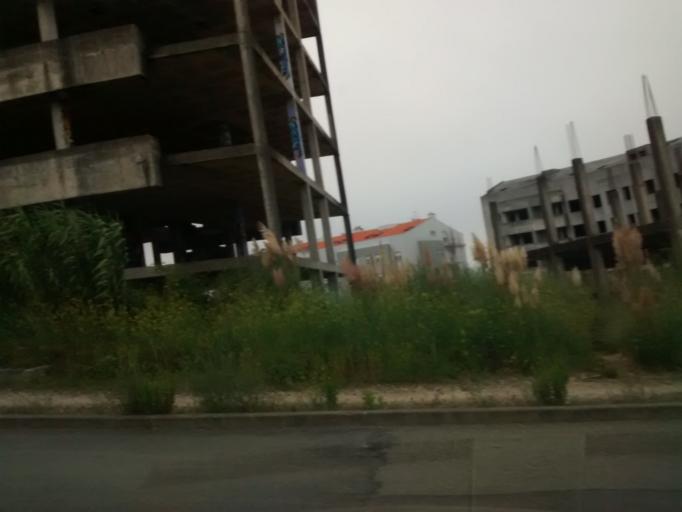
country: PT
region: Aveiro
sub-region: Aveiro
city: Aveiro
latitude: 40.6500
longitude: -8.6443
